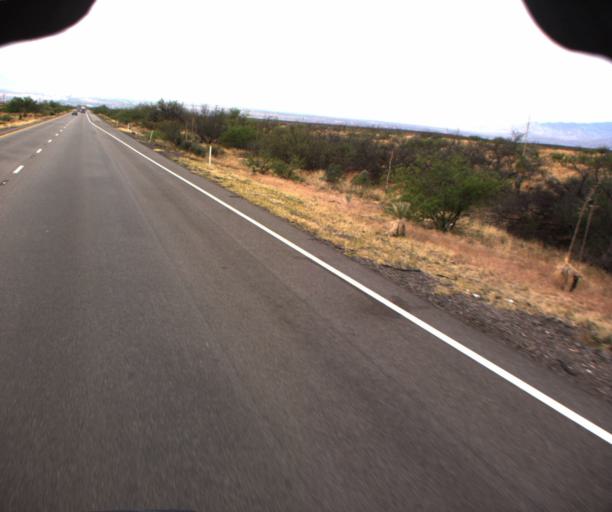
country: US
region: Arizona
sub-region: Cochise County
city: Saint David
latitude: 31.9909
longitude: -110.1814
